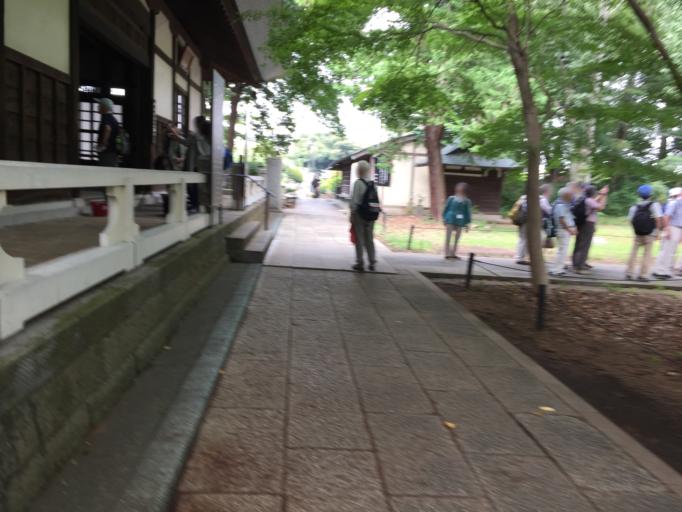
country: JP
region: Tokyo
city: Tokyo
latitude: 35.6084
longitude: 139.6604
